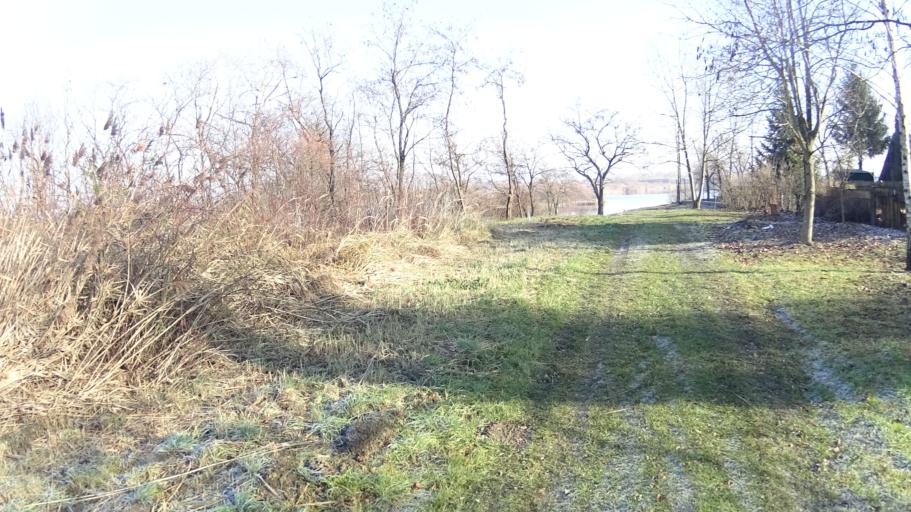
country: HU
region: Borsod-Abauj-Zemplen
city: Nyekladhaza
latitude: 47.9898
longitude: 20.8598
